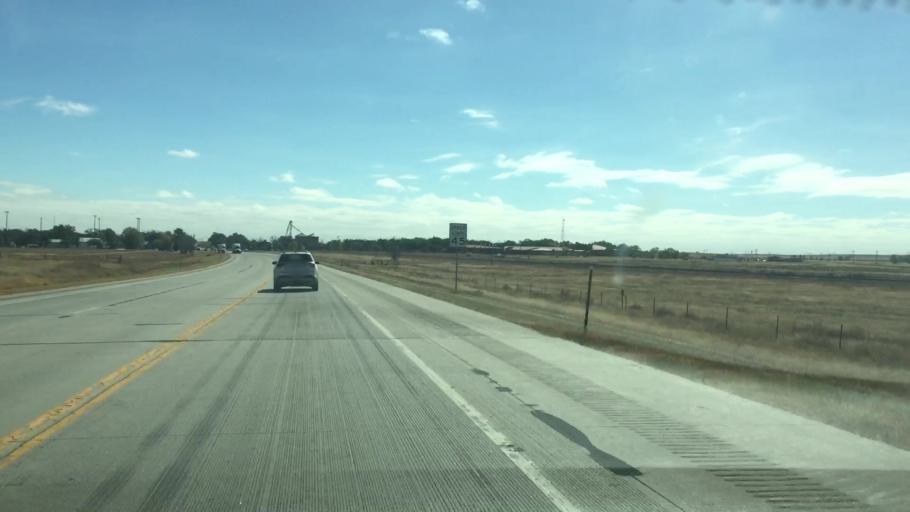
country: US
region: Colorado
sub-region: Lincoln County
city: Hugo
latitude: 39.1384
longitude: -103.4814
